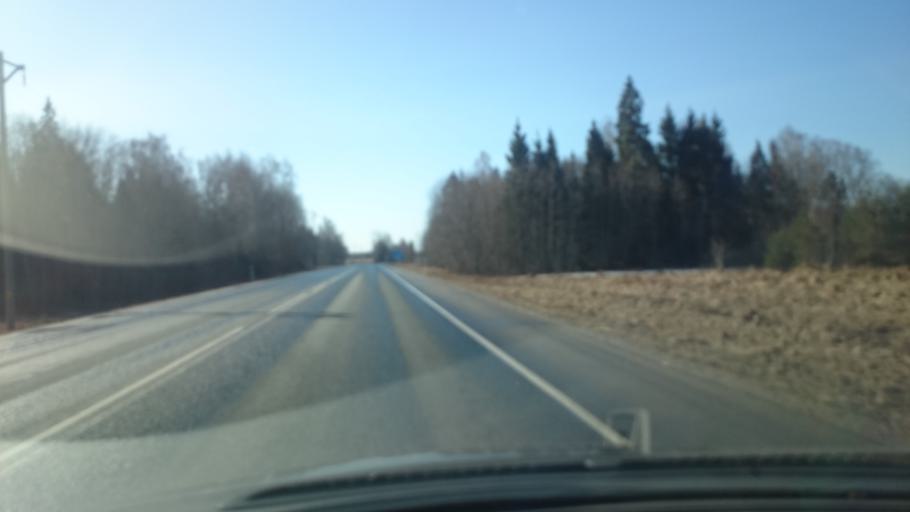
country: EE
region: Raplamaa
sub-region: Rapla vald
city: Rapla
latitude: 59.0453
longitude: 24.8387
